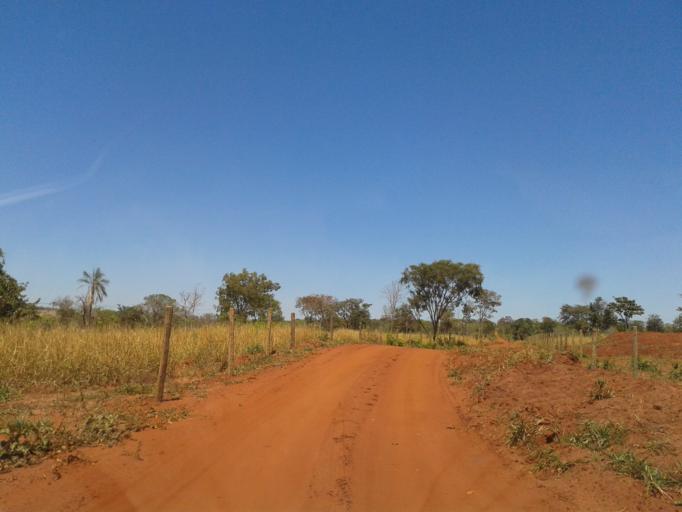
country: BR
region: Minas Gerais
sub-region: Ituiutaba
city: Ituiutaba
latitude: -19.0884
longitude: -49.2645
